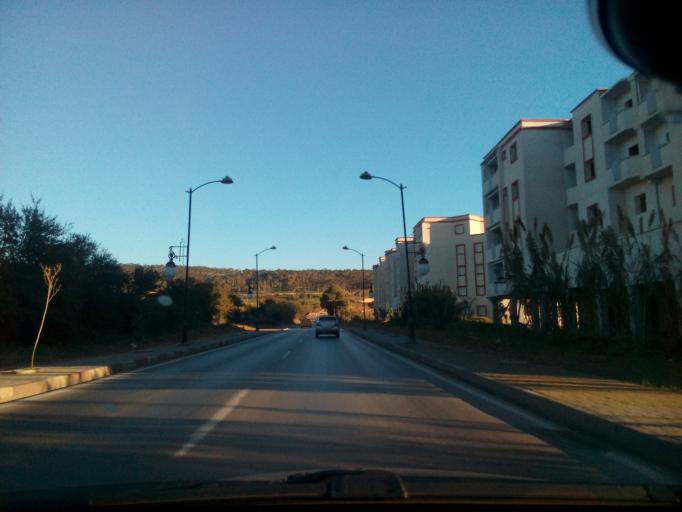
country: DZ
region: Mostaganem
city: Mostaganem
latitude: 35.7755
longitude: 0.1971
